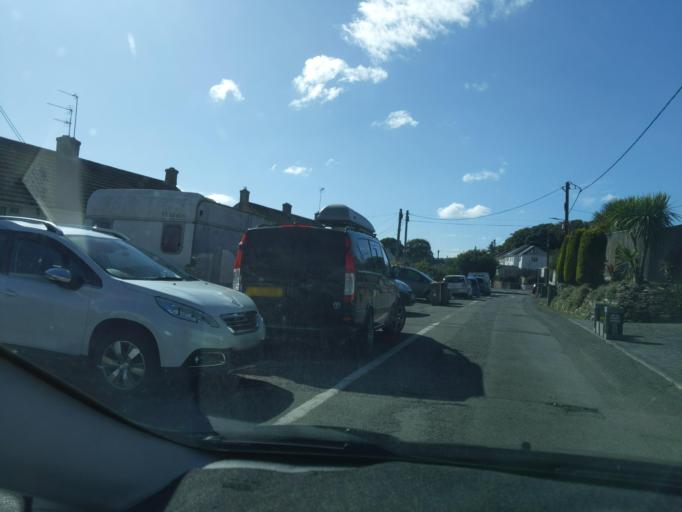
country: GB
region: England
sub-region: Plymouth
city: Plymstock
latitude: 50.3572
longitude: -4.0701
